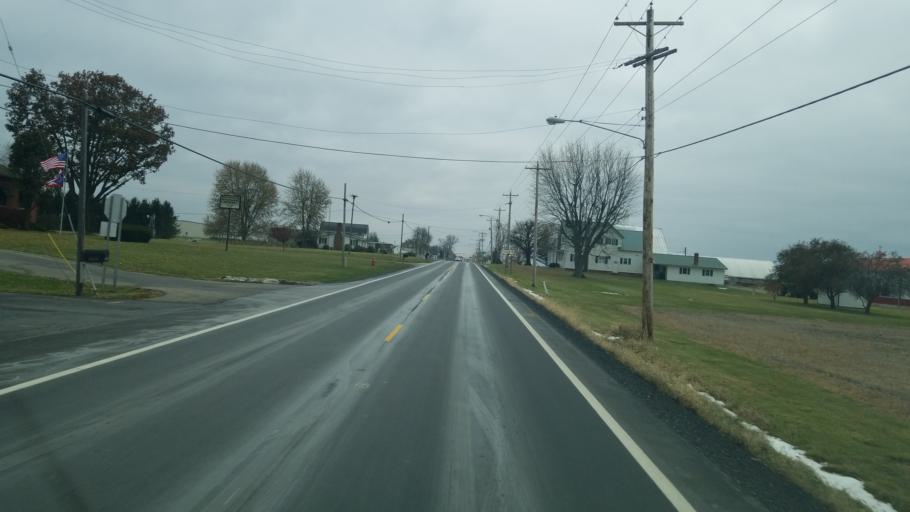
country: US
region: Ohio
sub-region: Crawford County
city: Bucyrus
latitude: 40.8374
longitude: -82.9706
